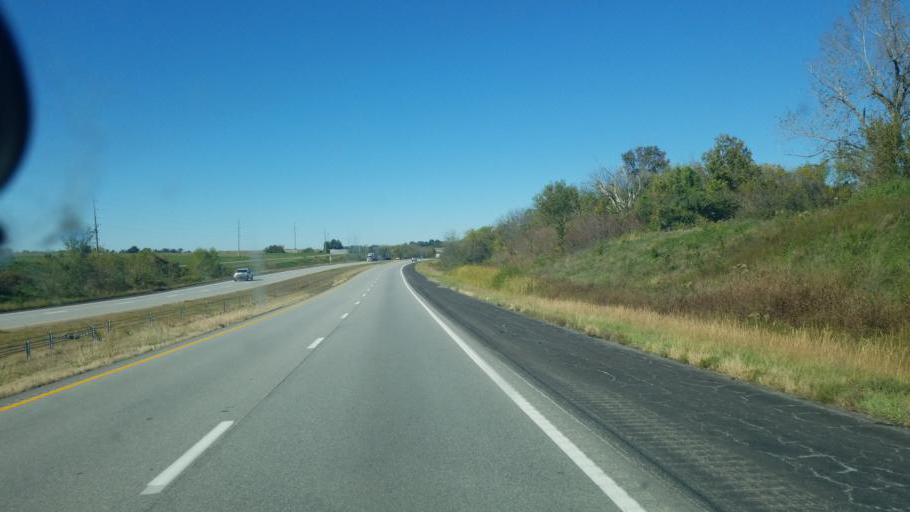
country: US
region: Missouri
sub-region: Lafayette County
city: Concordia
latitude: 38.9898
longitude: -93.6385
